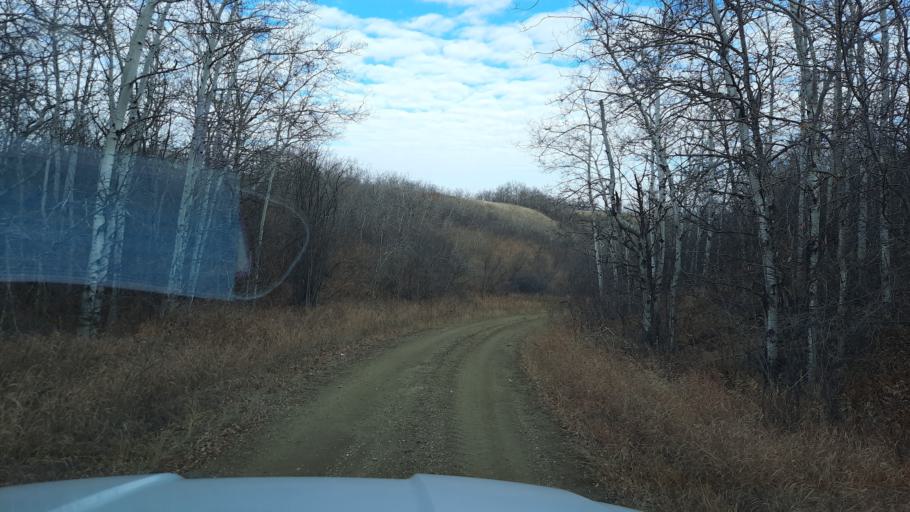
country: CA
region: Saskatchewan
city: Pilot Butte
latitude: 50.7743
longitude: -104.2158
